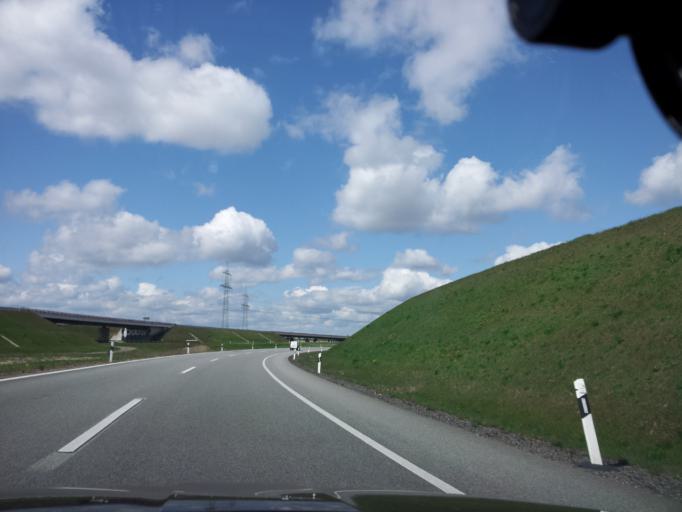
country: DE
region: Brandenburg
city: Ahrensfelde
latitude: 52.6151
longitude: 13.5628
